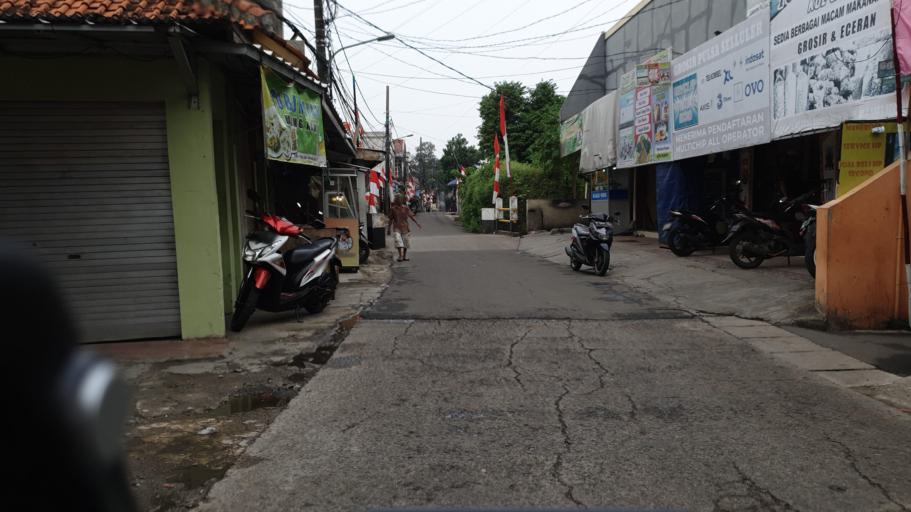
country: ID
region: West Java
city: Pamulang
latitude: -6.3323
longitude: 106.7686
